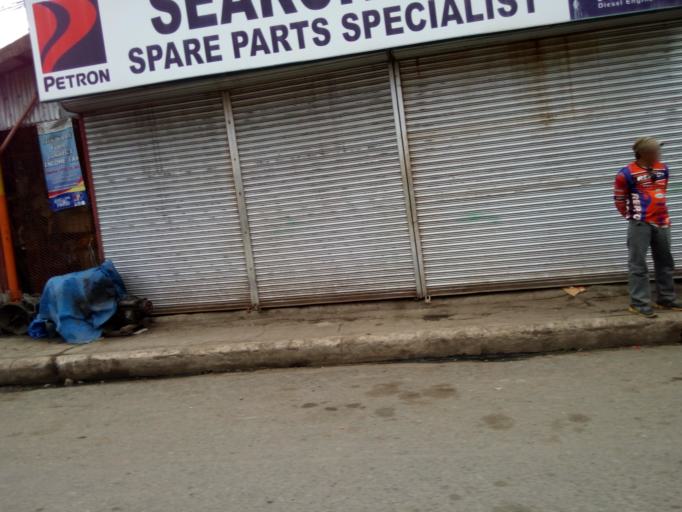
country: PH
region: Caraga
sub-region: Province of Surigao del Norte
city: Surigao
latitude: 9.7855
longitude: 125.4907
